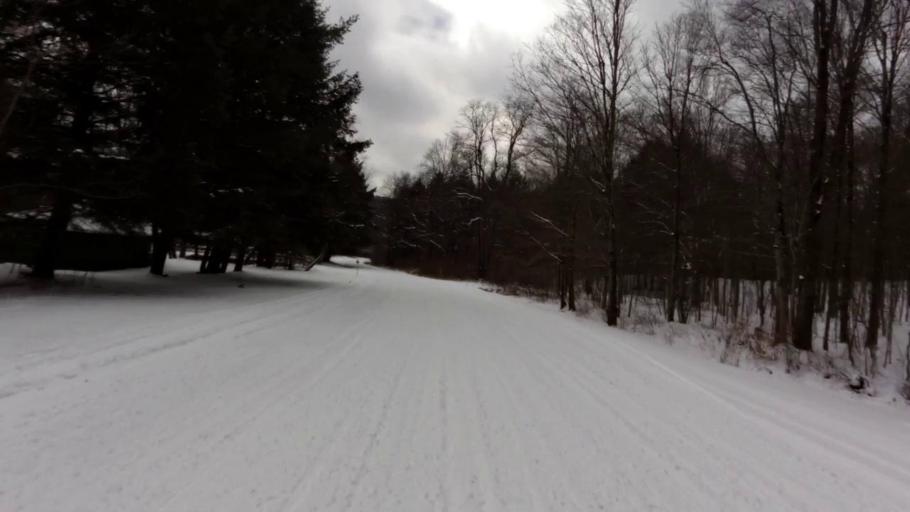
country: US
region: New York
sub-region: Cattaraugus County
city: Salamanca
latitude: 42.0161
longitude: -78.8232
